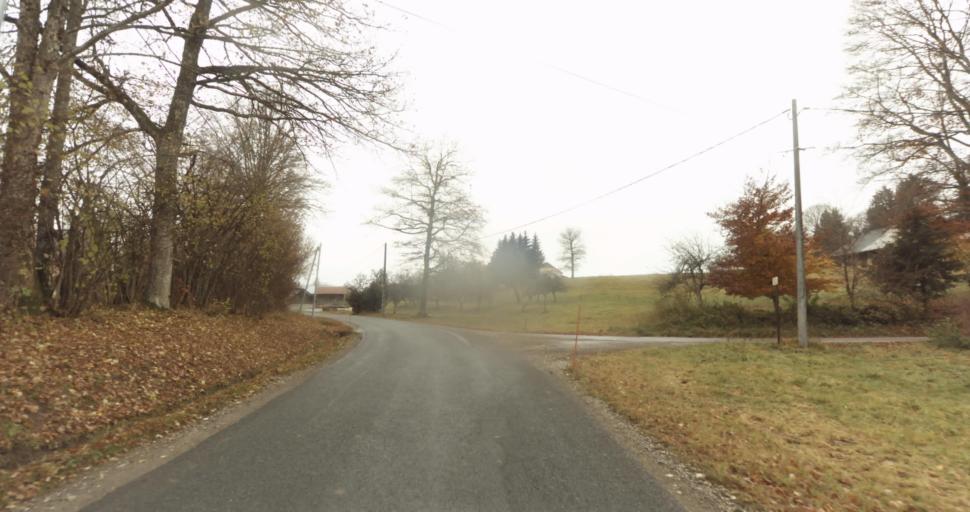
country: FR
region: Rhone-Alpes
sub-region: Departement de la Haute-Savoie
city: Evires
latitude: 46.0608
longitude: 6.2074
